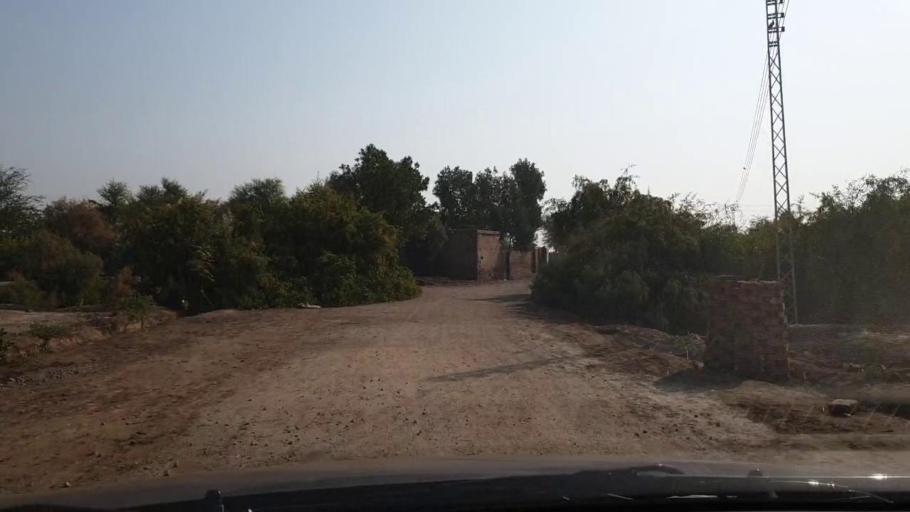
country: PK
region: Sindh
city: Sanghar
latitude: 25.9772
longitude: 68.9768
